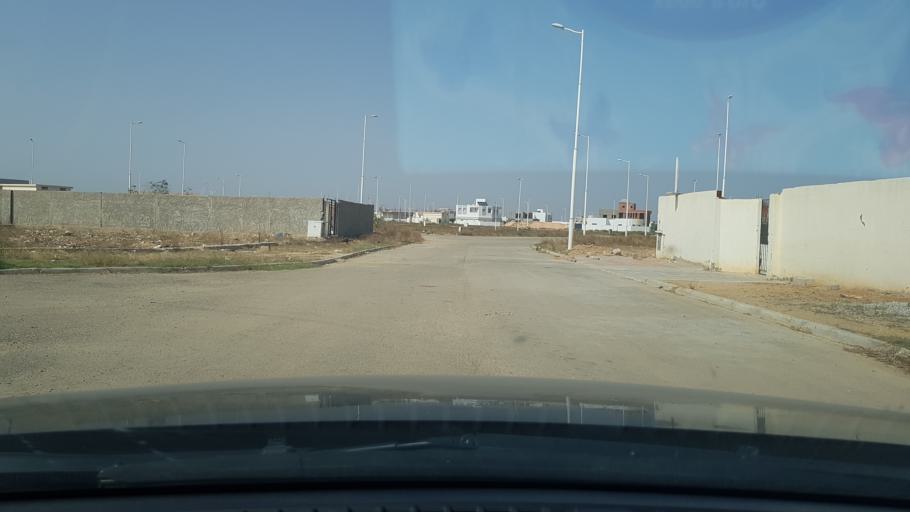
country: TN
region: Safaqis
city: Al Qarmadah
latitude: 34.8325
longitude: 10.7533
